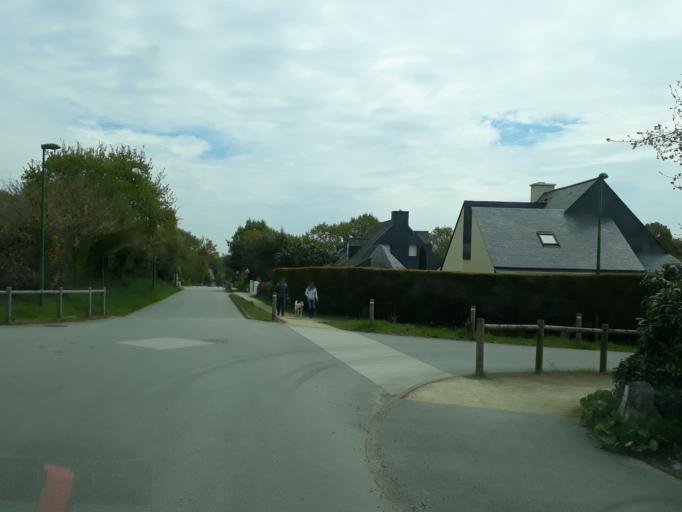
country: FR
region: Brittany
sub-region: Departement du Morbihan
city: Surzur
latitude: 47.5819
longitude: -2.6421
